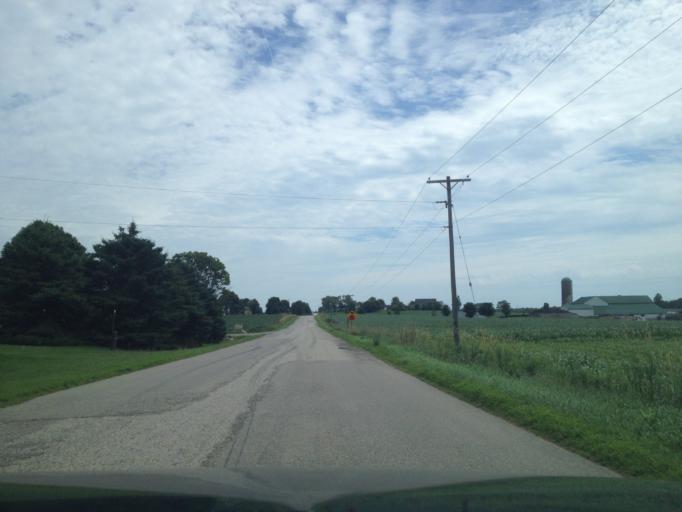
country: CA
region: Ontario
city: Ingersoll
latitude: 42.9811
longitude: -80.7400
